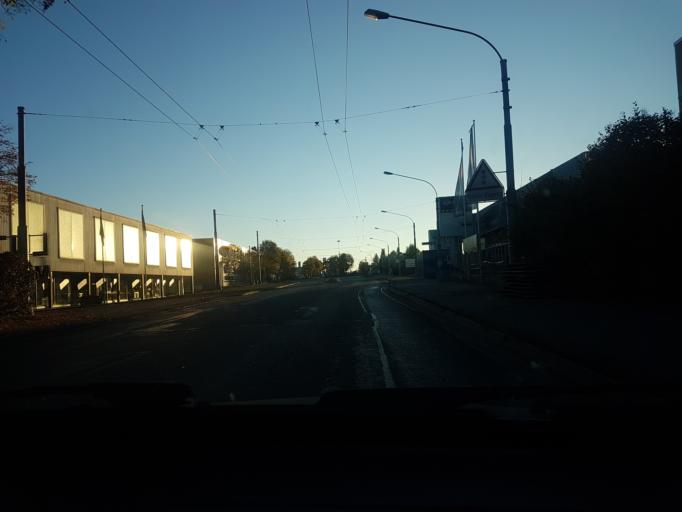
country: CH
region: Neuchatel
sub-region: La Chaux-de-Fonds District
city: La Chaux-de-Fonds
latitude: 47.0872
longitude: 6.8029
